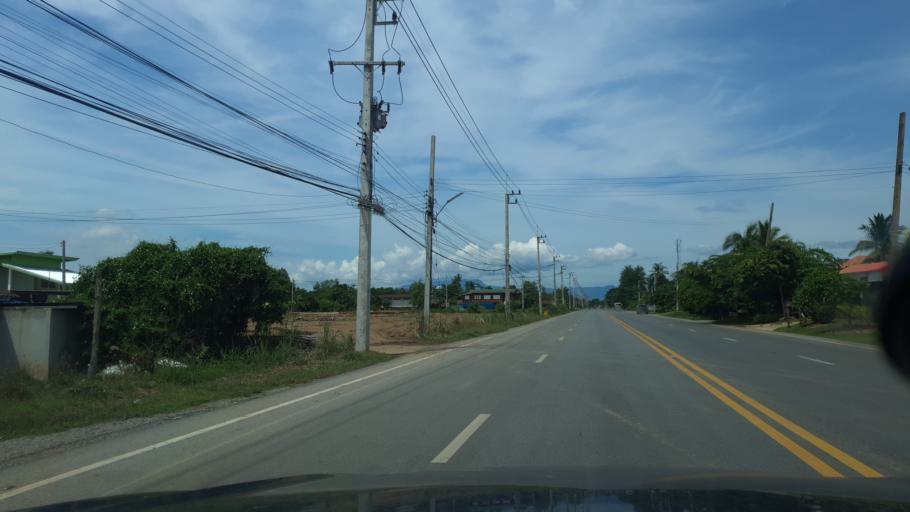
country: TH
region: Sukhothai
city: Sukhothai
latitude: 17.0578
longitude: 99.8255
